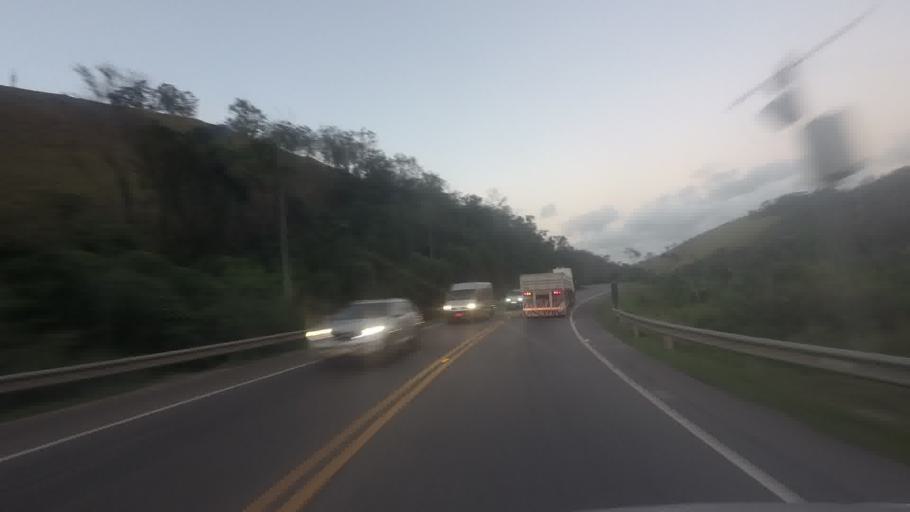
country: BR
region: Espirito Santo
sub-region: Iconha
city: Iconha
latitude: -20.8296
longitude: -40.8583
